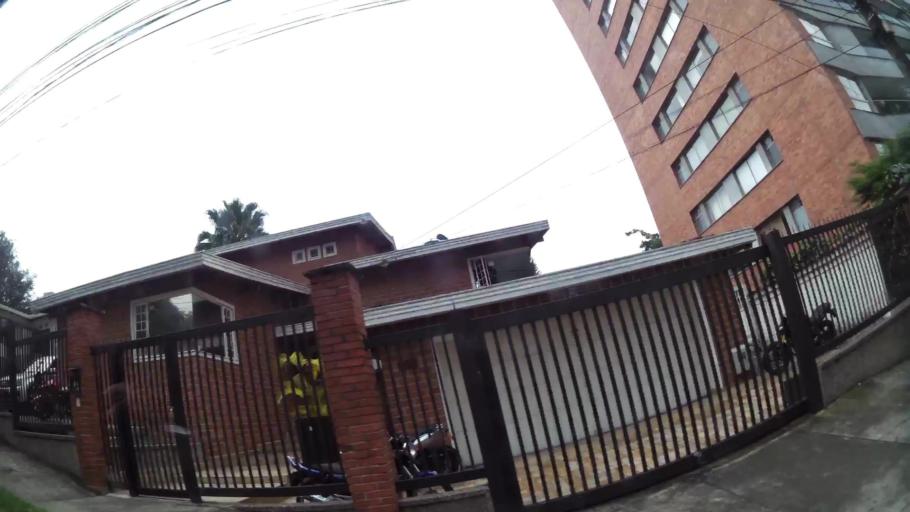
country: CO
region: Antioquia
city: Medellin
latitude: 6.2123
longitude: -75.5635
